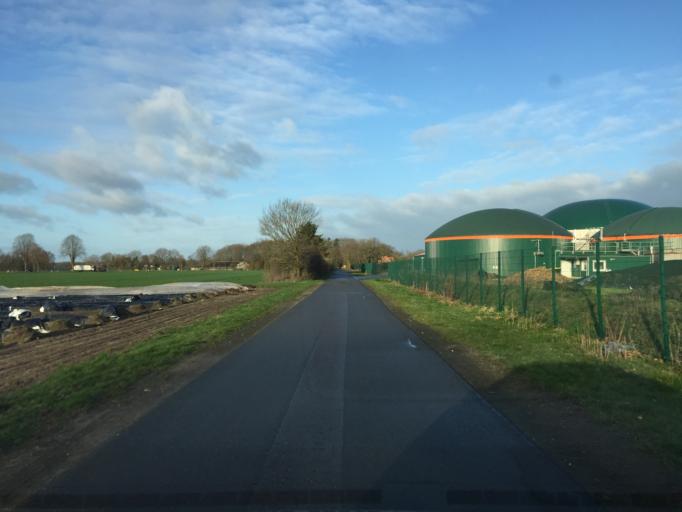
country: DE
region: Lower Saxony
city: Steyerberg
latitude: 52.5926
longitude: 8.9851
